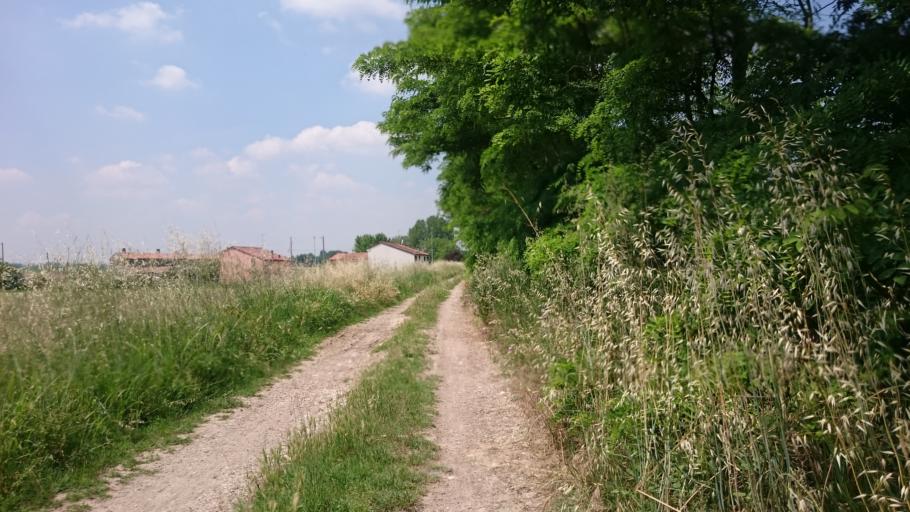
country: IT
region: Lombardy
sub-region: Provincia di Mantova
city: Lunetta-Frassino
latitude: 45.1281
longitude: 10.8254
